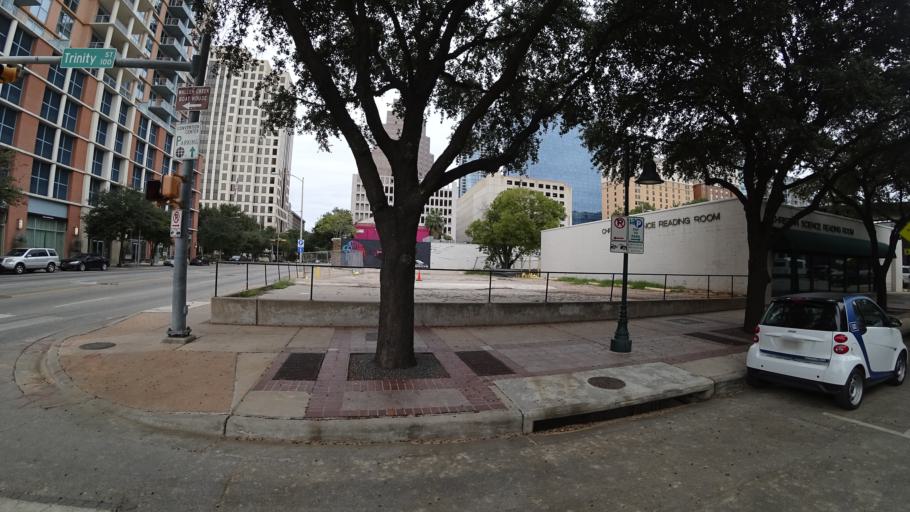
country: US
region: Texas
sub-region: Travis County
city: Austin
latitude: 30.2625
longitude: -97.7410
